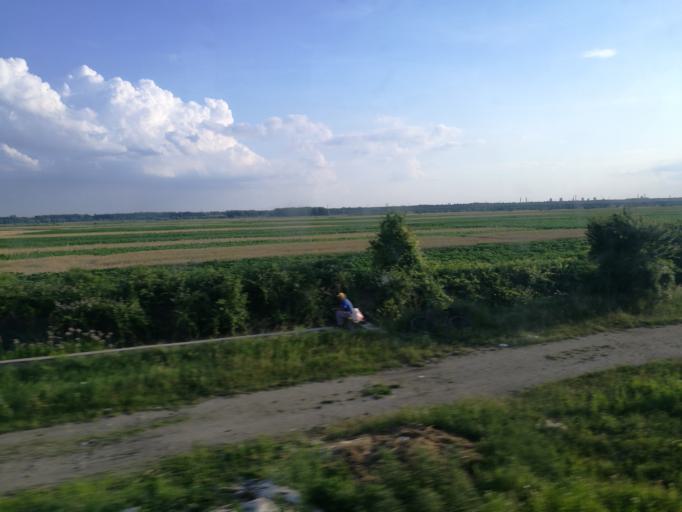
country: RO
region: Arges
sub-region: Comuna Calinesti
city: Vranesti
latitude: 44.8248
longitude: 25.0147
